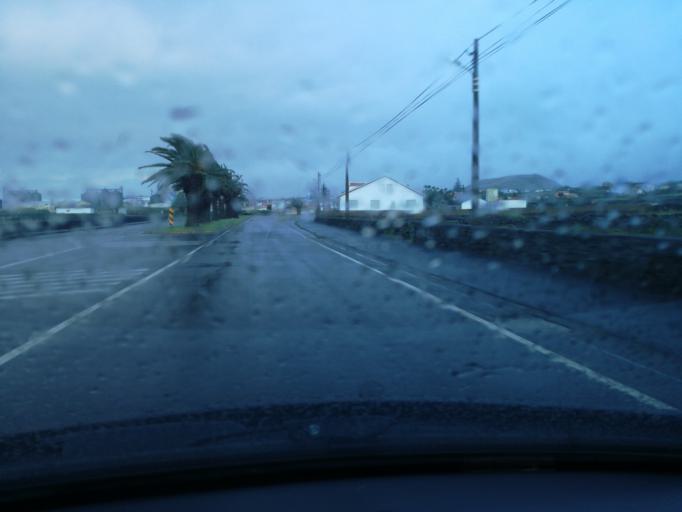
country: PT
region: Azores
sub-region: Praia da Vitoria
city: Praia da Vitoria
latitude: 38.7123
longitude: -27.0621
